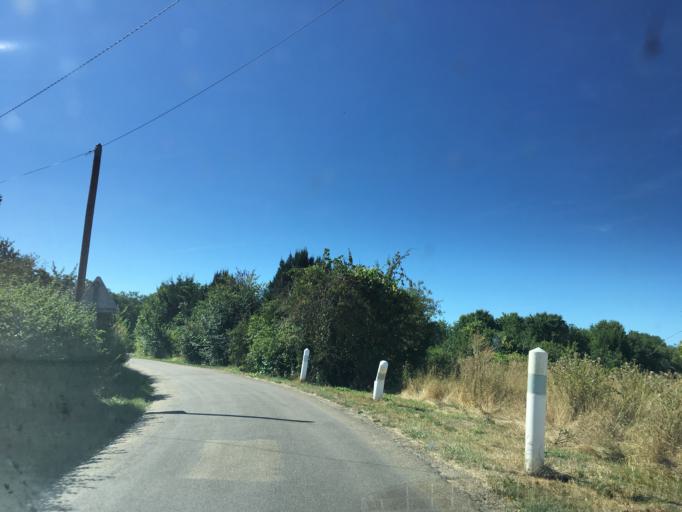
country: FR
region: Bourgogne
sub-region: Departement de l'Yonne
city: Fleury-la-Vallee
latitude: 47.8905
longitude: 3.4390
